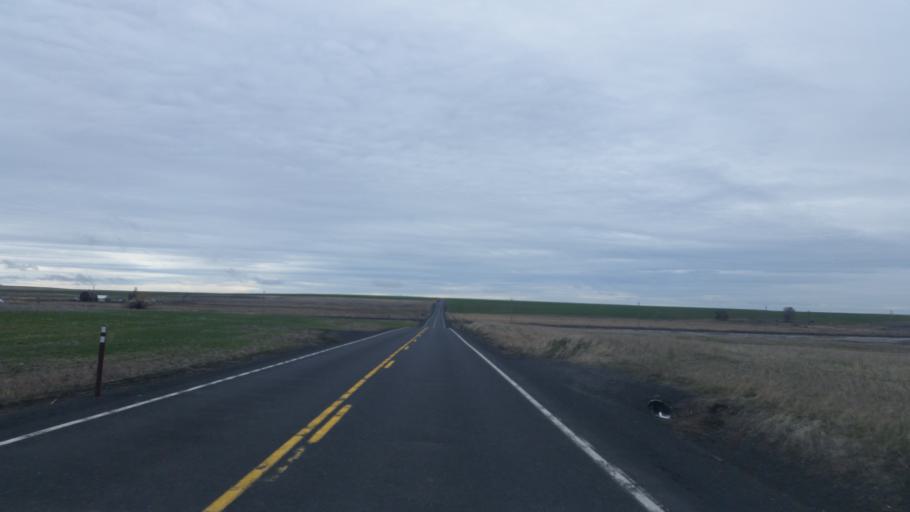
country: US
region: Washington
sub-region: Okanogan County
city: Coulee Dam
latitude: 47.7466
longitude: -118.7218
